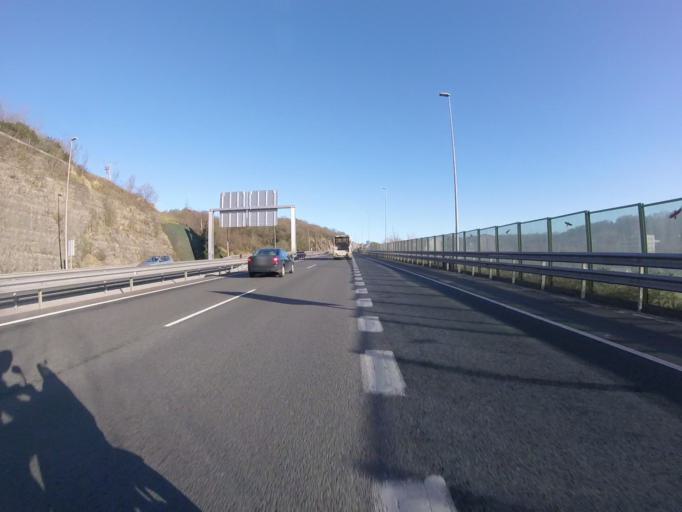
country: ES
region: Basque Country
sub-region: Provincia de Guipuzcoa
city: Astigarraga
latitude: 43.2914
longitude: -1.9567
